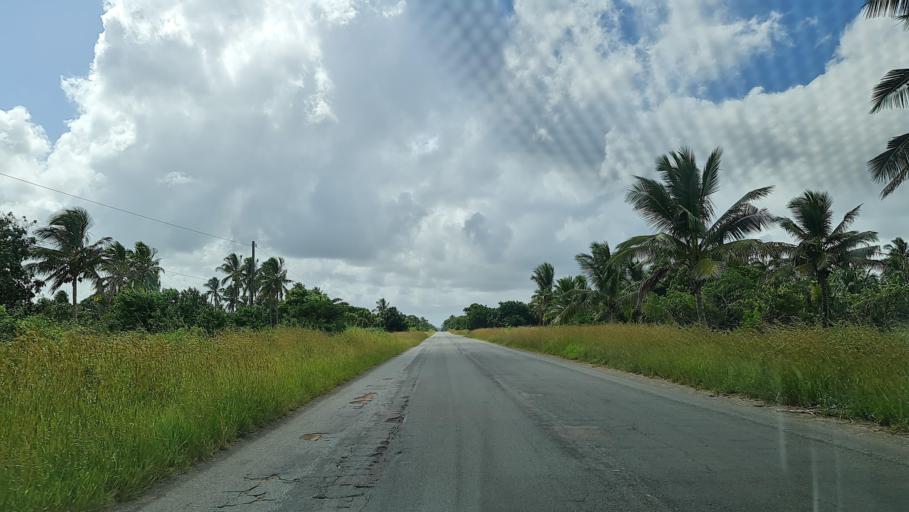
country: MZ
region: Gaza
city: Manjacaze
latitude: -24.6812
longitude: 34.6073
